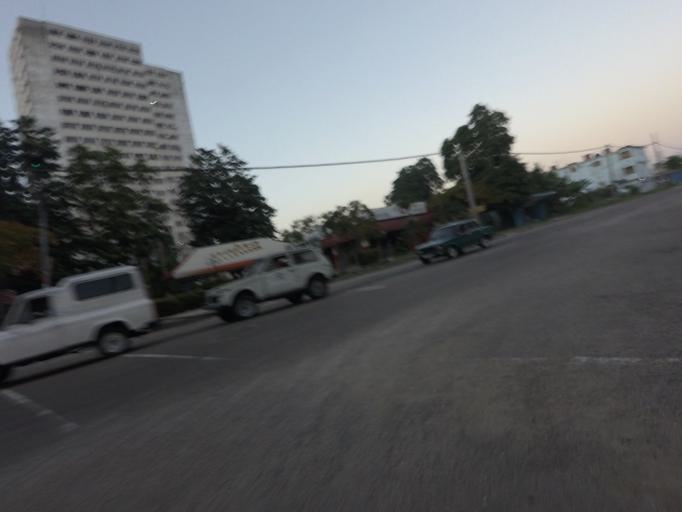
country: CU
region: La Habana
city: Havana
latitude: 23.1233
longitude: -82.3741
